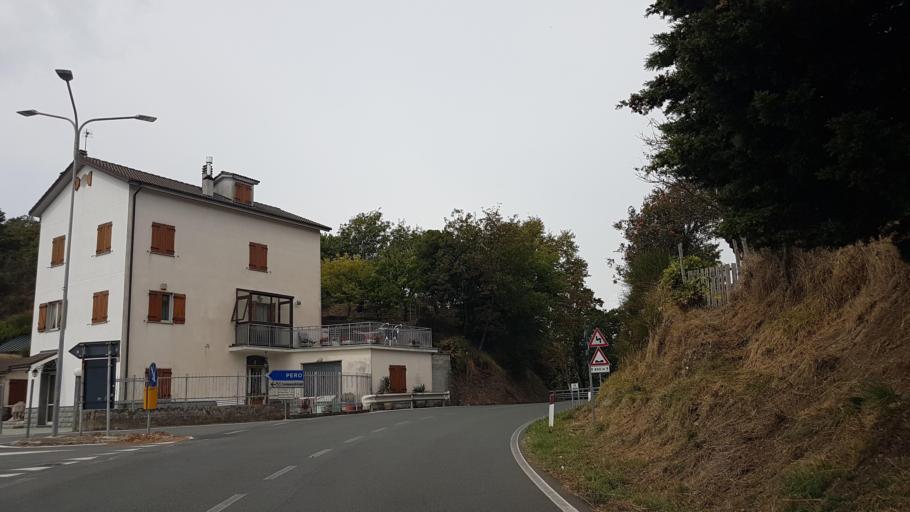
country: IT
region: Liguria
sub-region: Provincia di Genova
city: Moneglia
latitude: 44.2551
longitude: 9.4785
